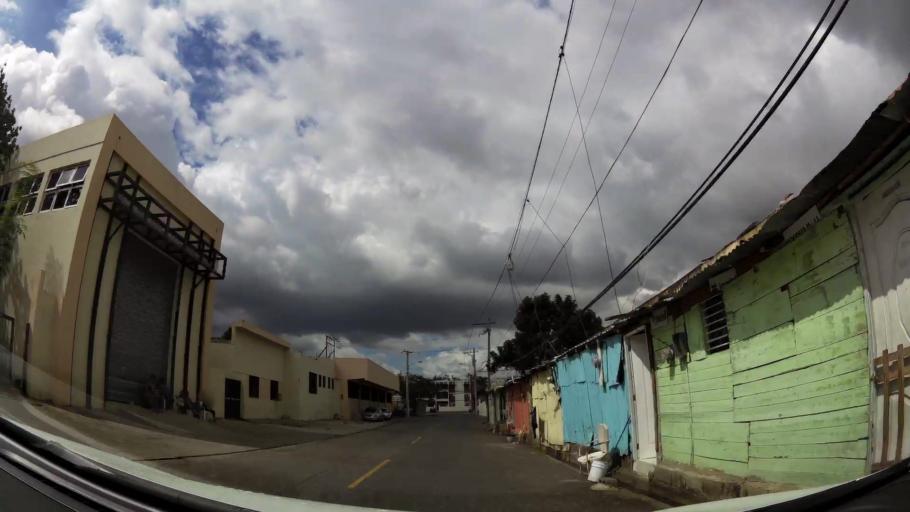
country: DO
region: Nacional
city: La Agustina
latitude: 18.4924
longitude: -69.9277
